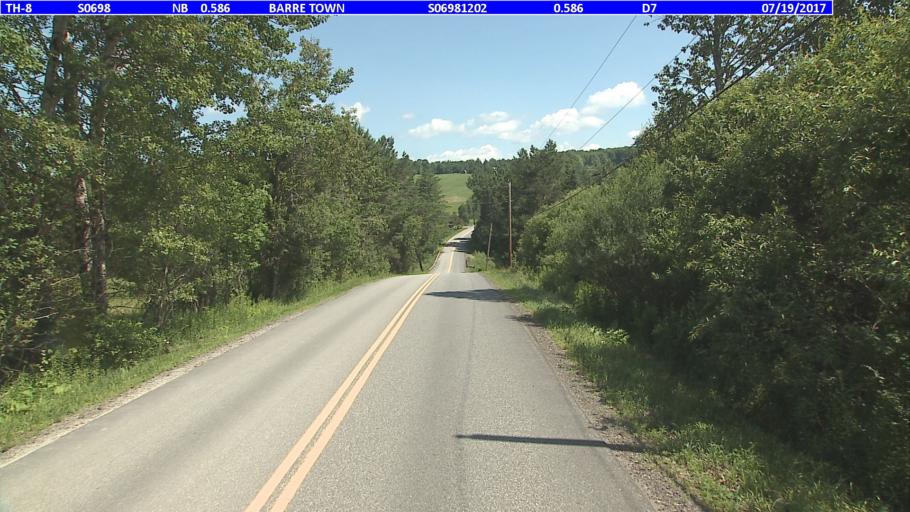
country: US
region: Vermont
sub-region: Washington County
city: Barre
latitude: 44.2270
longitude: -72.4592
